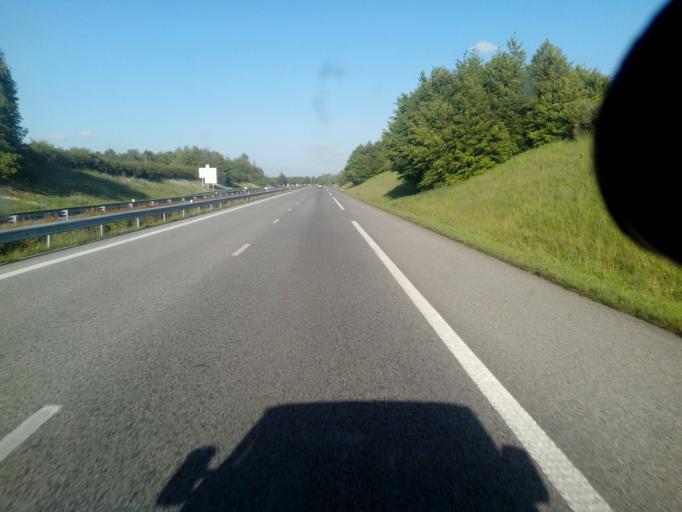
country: FR
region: Haute-Normandie
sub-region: Departement de la Seine-Maritime
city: Valliquerville
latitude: 49.6394
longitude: 0.7093
